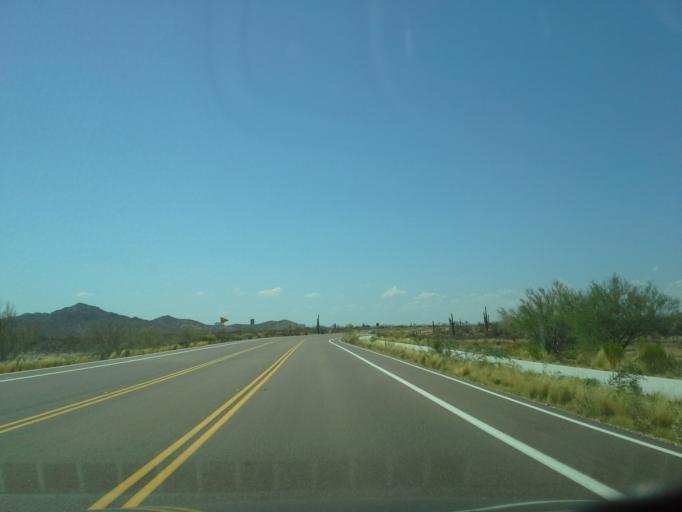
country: US
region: Arizona
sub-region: Maricopa County
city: Cave Creek
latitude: 33.7630
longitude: -112.0458
